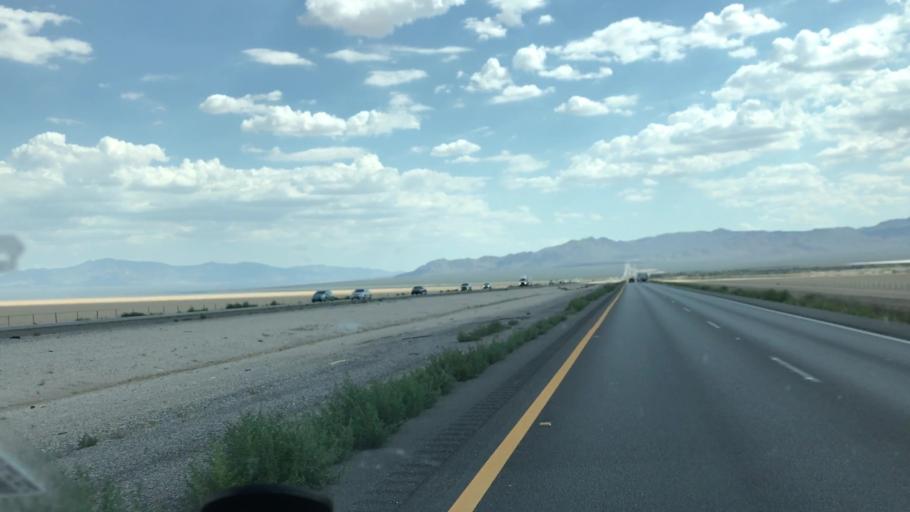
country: US
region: Nevada
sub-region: Clark County
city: Sandy Valley
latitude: 35.5812
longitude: -115.4027
